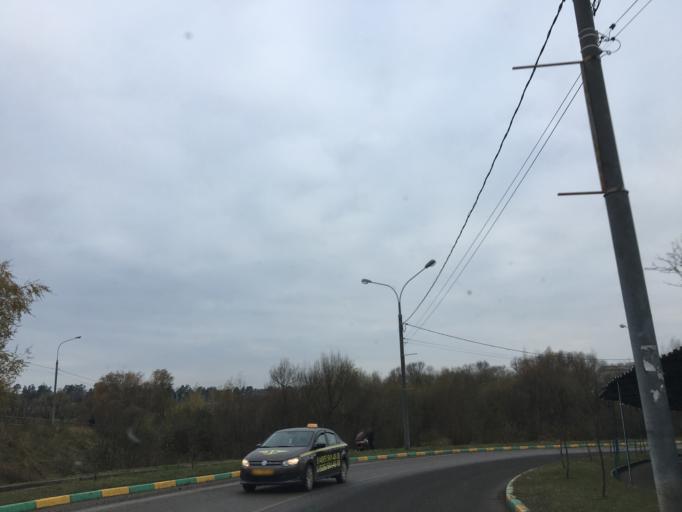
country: RU
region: Moskovskaya
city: Vidnoye
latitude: 55.5446
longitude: 37.6988
